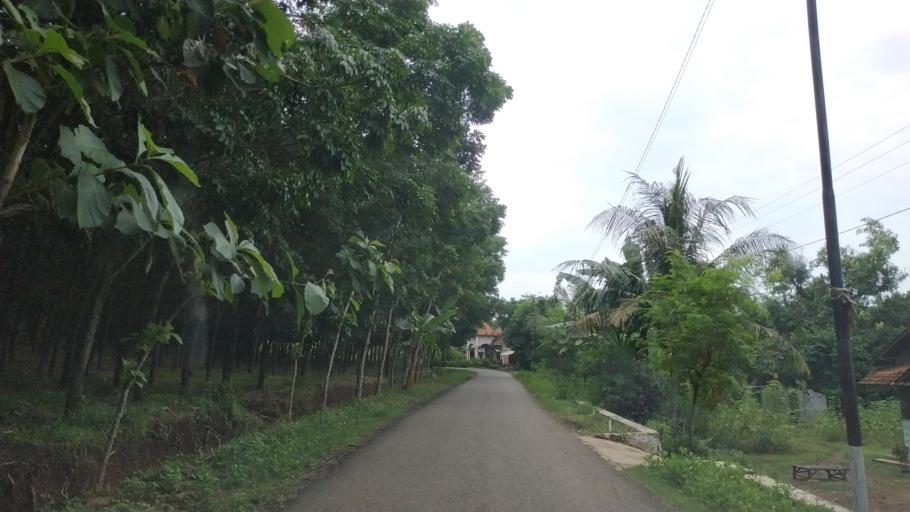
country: ID
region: Central Java
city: Krajan Tegalombo
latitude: -6.4372
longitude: 110.9815
